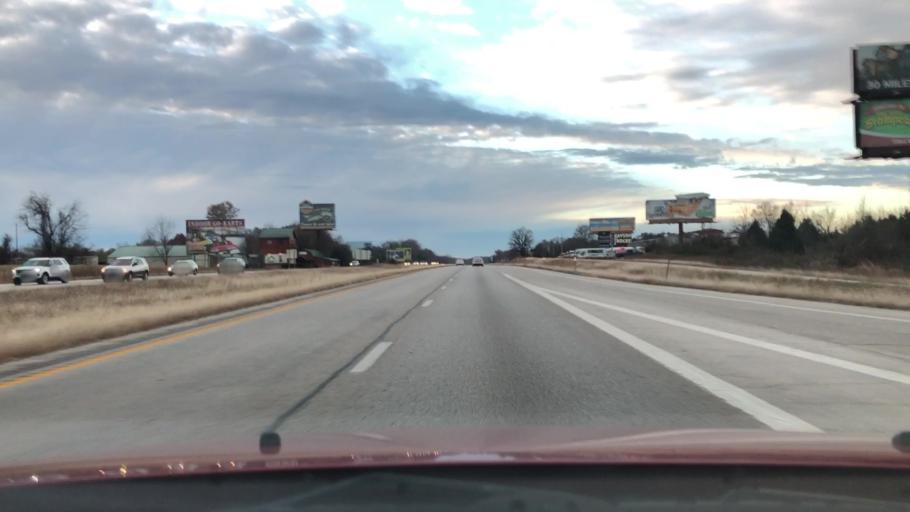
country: US
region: Missouri
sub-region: Christian County
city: Ozark
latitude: 36.9407
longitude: -93.2322
